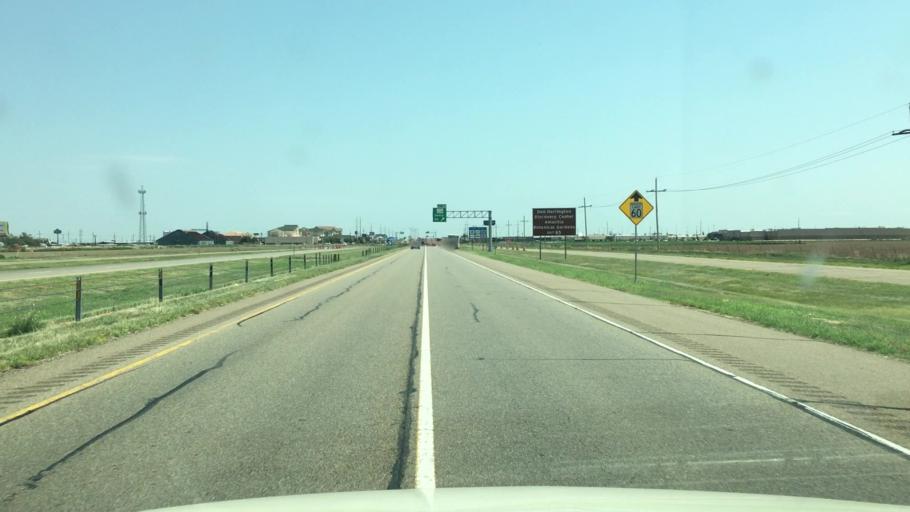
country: US
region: Texas
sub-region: Potter County
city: Bushland
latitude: 35.1873
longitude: -101.9502
